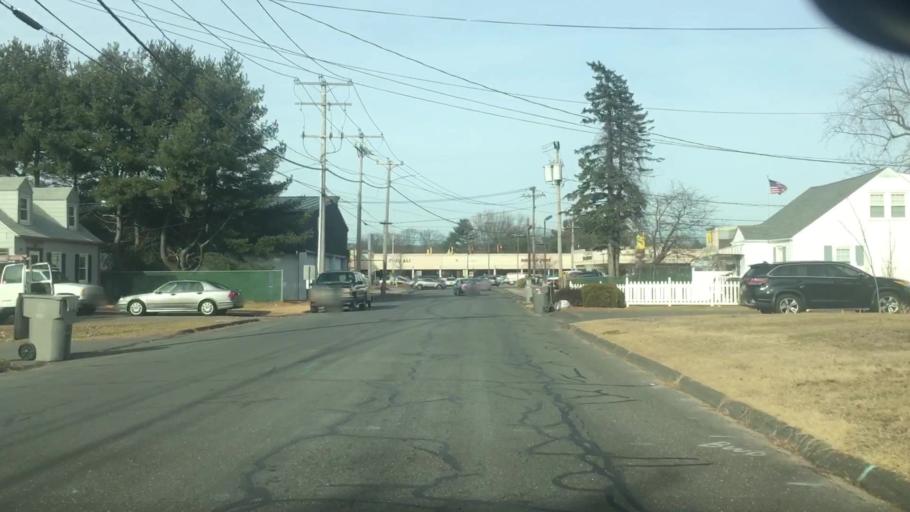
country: US
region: Connecticut
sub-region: Hartford County
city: Bristol
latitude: 41.6896
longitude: -72.9226
